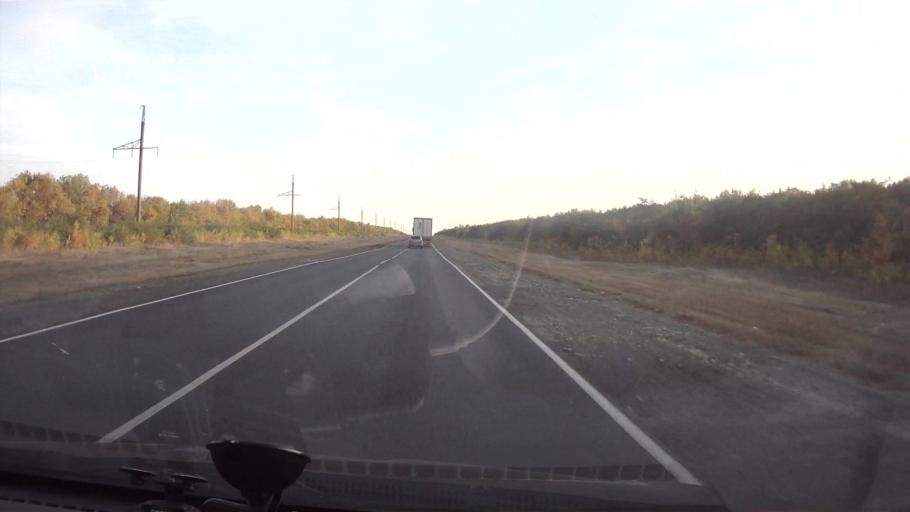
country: RU
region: Saratov
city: Krasnoarmeysk
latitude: 51.1396
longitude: 45.6500
